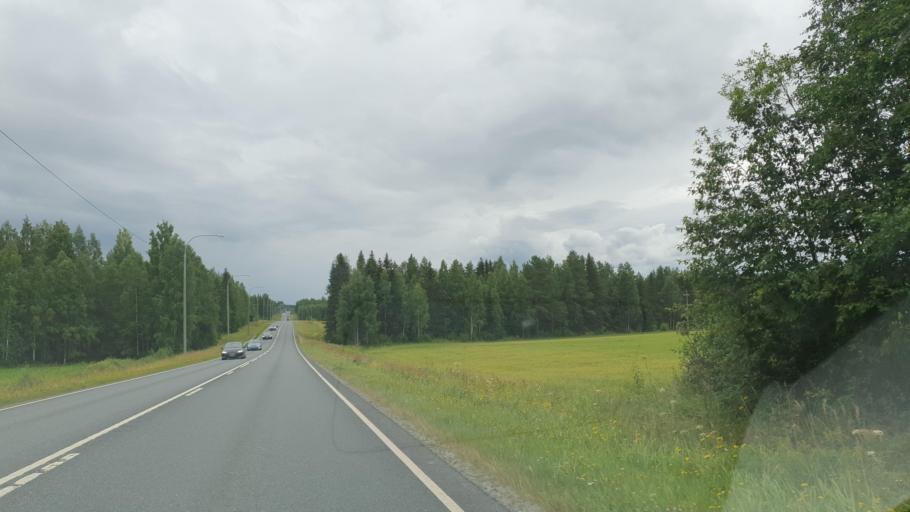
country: FI
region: Northern Savo
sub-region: Ylae-Savo
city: Lapinlahti
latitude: 63.3233
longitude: 27.4424
